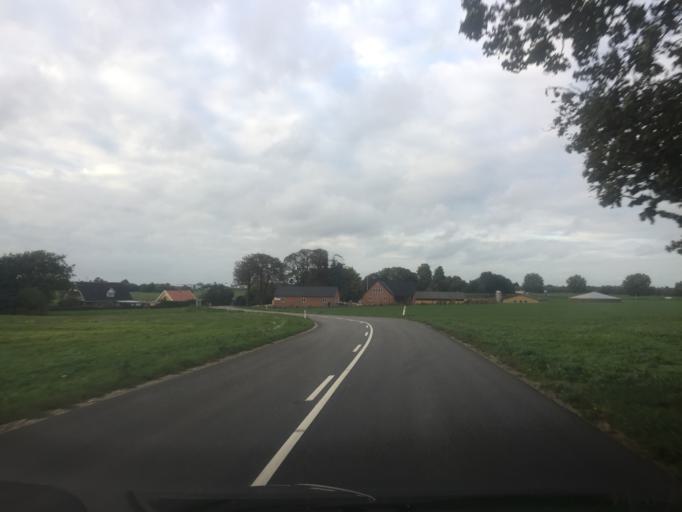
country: DK
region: Zealand
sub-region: Solrod Kommune
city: Havdrup
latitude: 55.5655
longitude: 12.1140
